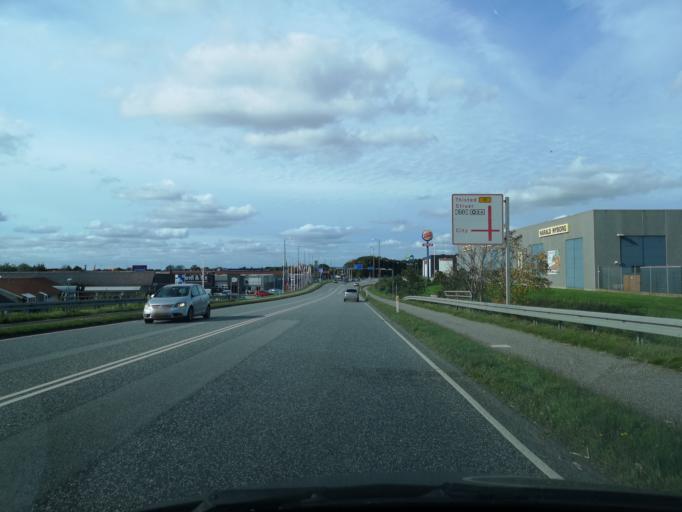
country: DK
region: Central Jutland
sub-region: Holstebro Kommune
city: Holstebro
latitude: 56.3752
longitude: 8.6206
